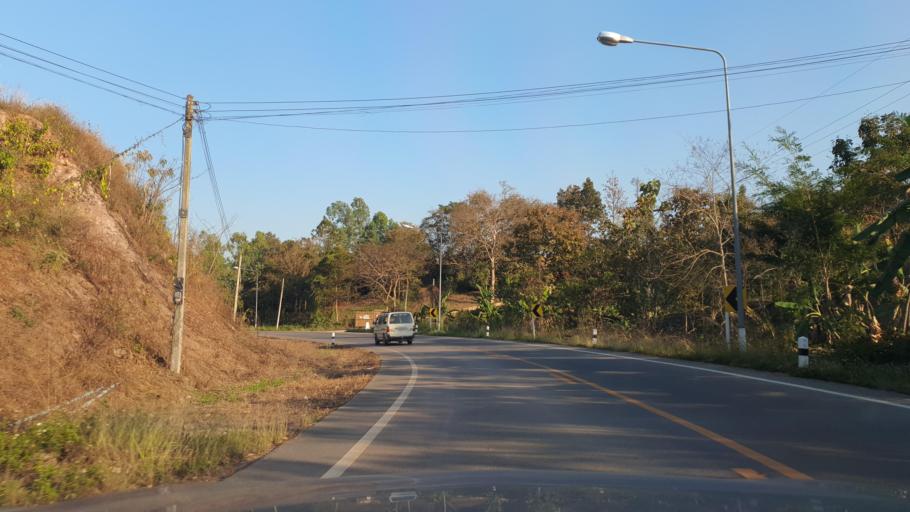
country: TH
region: Chiang Rai
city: Mae Lao
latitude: 19.8340
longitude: 99.6836
